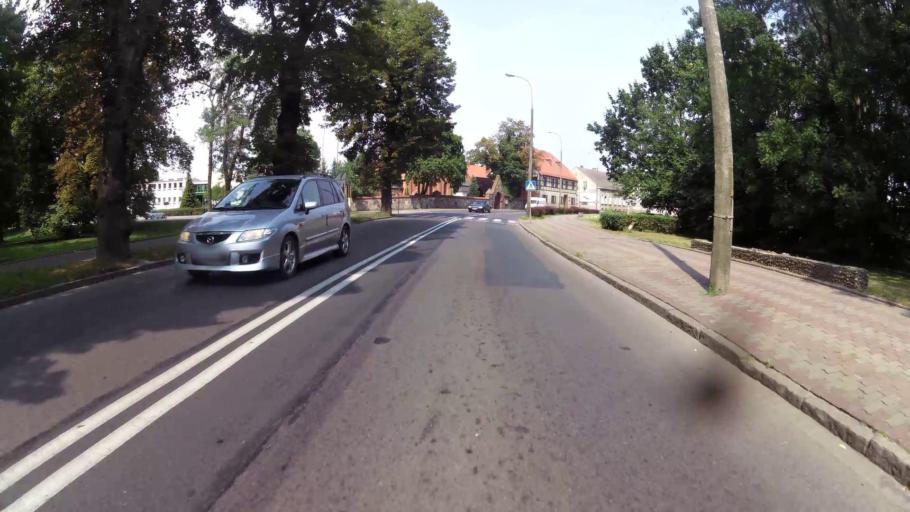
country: PL
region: West Pomeranian Voivodeship
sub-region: Powiat mysliborski
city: Mysliborz
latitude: 52.9216
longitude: 14.8625
